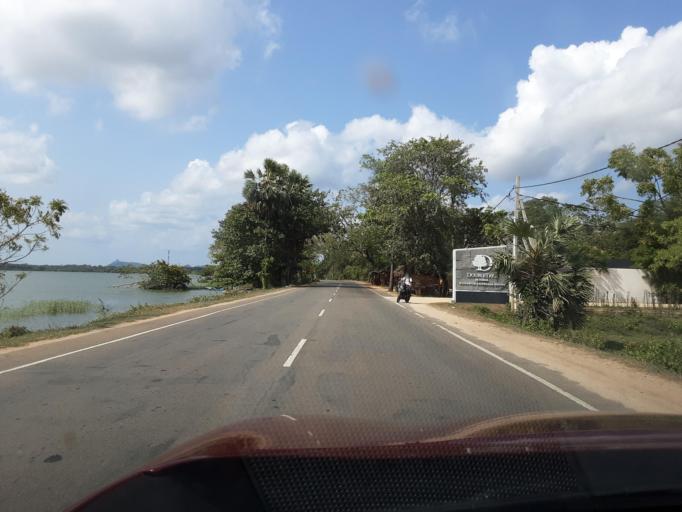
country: LK
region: Southern
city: Tangalla
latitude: 6.2830
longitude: 81.2309
